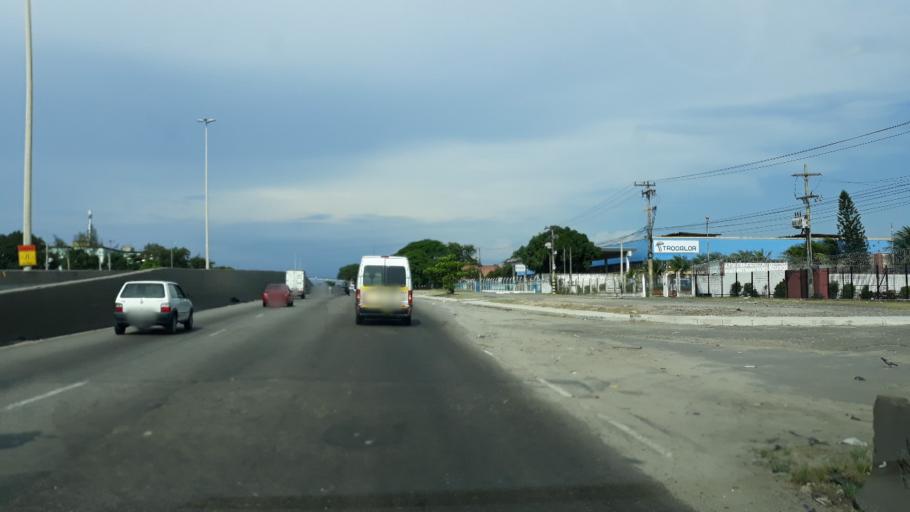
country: BR
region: Rio de Janeiro
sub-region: Sao Joao De Meriti
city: Sao Joao de Meriti
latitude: -22.8327
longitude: -43.3550
